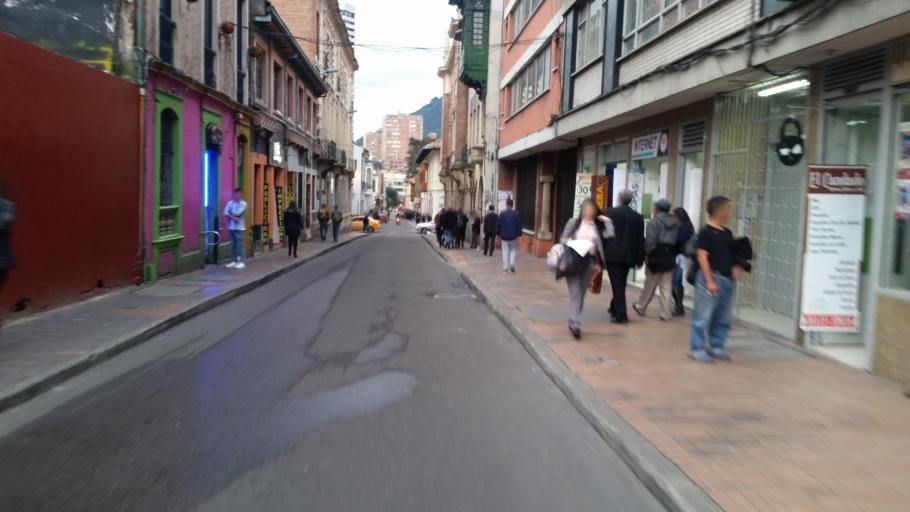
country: CO
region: Bogota D.C.
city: Bogota
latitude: 4.5983
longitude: -74.0730
